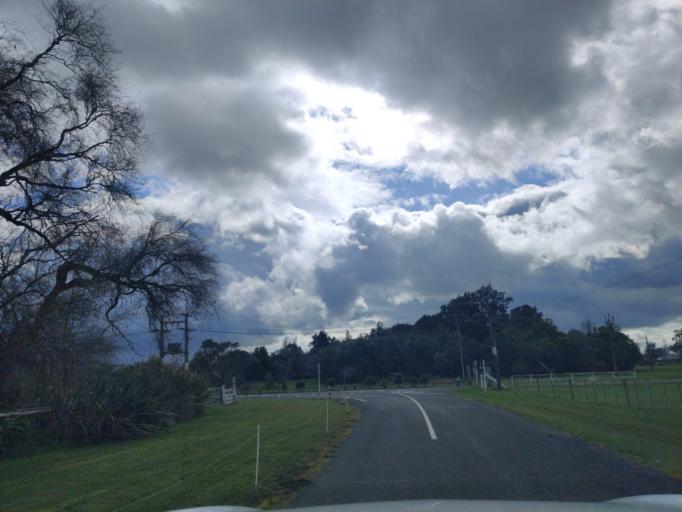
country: NZ
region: Manawatu-Wanganui
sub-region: Palmerston North City
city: Palmerston North
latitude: -40.2333
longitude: 175.5574
